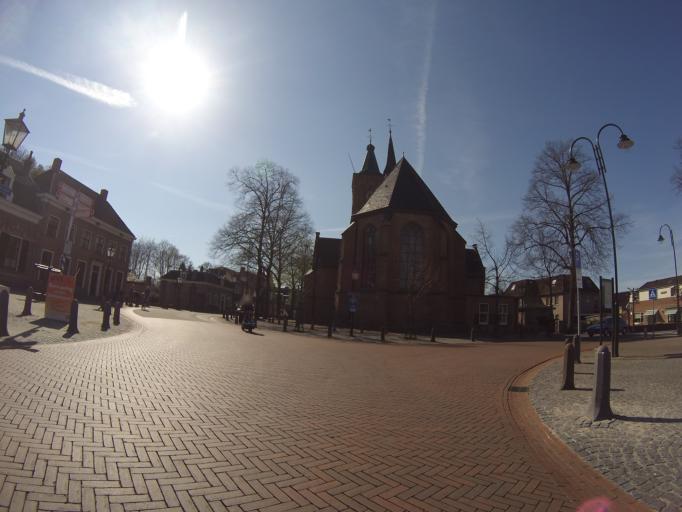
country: NL
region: Utrecht
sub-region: Gemeente Utrechtse Heuvelrug
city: Overberg
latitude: 52.0796
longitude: 5.4900
